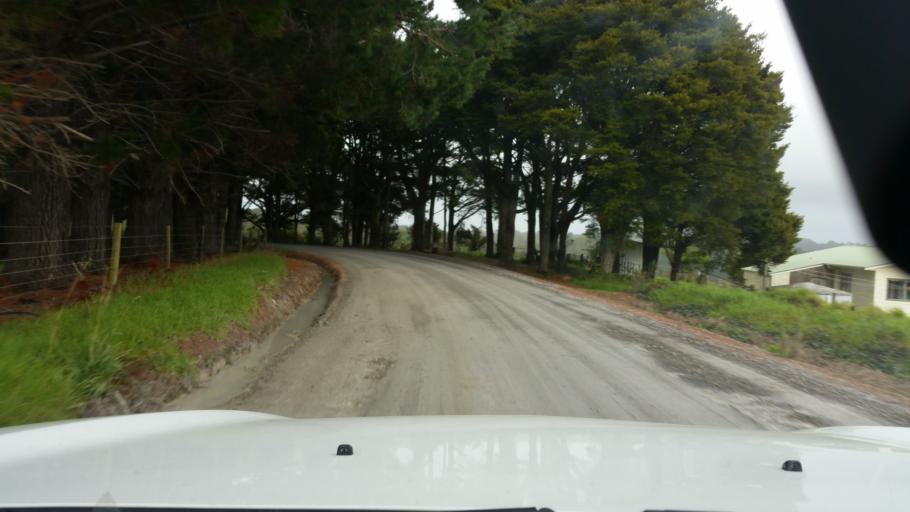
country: NZ
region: Northland
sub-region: Whangarei
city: Ngunguru
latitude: -35.7507
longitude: 174.4899
